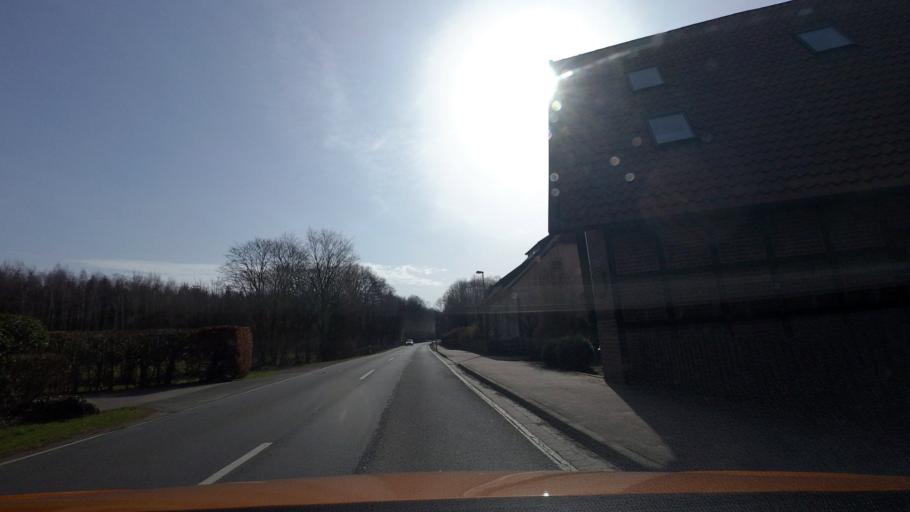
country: DE
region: Lower Saxony
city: Wiedensahl
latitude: 52.3715
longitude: 9.1283
